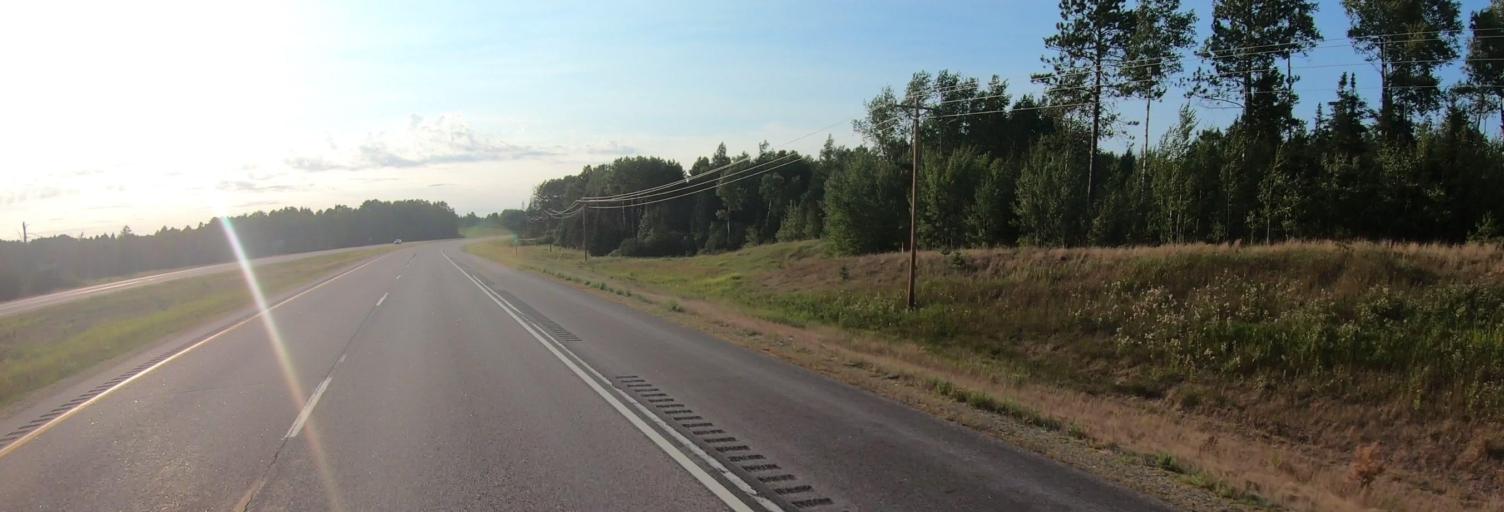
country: US
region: Minnesota
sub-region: Saint Louis County
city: Mountain Iron
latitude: 47.6687
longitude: -92.6303
